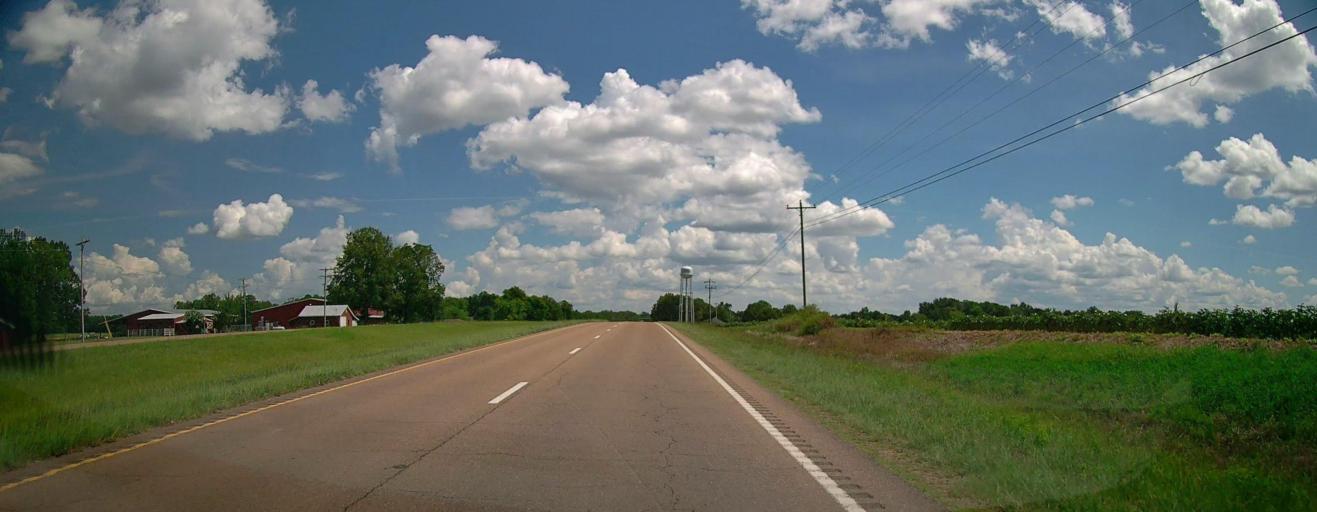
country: US
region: Mississippi
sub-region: Monroe County
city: Aberdeen
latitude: 33.7967
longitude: -88.4629
